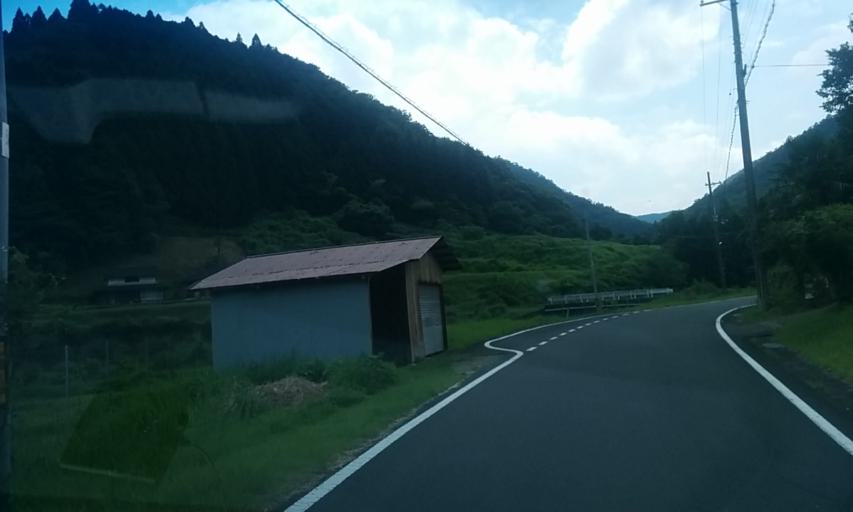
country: JP
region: Kyoto
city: Ayabe
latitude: 35.1920
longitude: 135.2171
